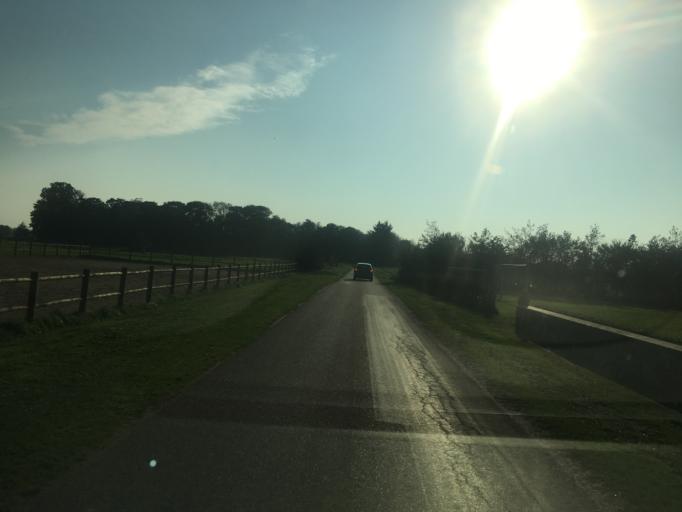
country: DE
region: Schleswig-Holstein
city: Bramstedtlund
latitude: 54.9231
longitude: 9.0535
